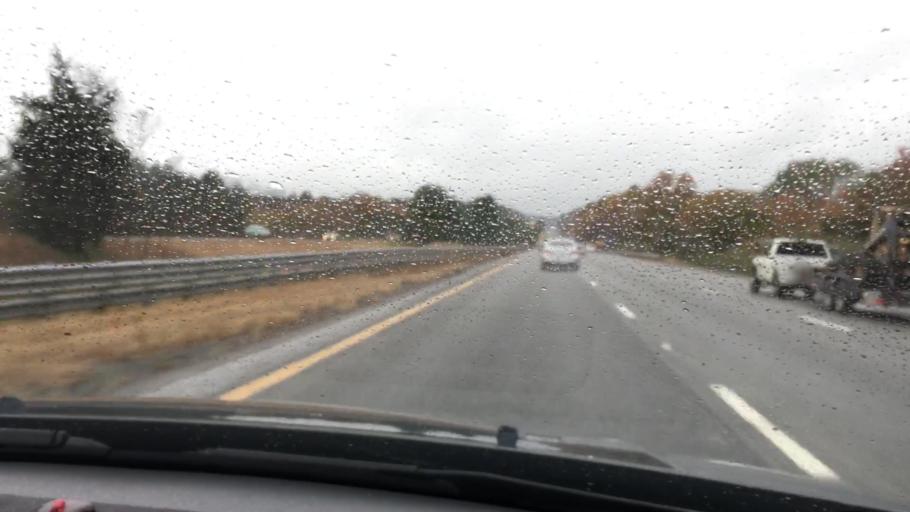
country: US
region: Massachusetts
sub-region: Middlesex County
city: Westford
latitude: 42.5566
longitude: -71.4470
